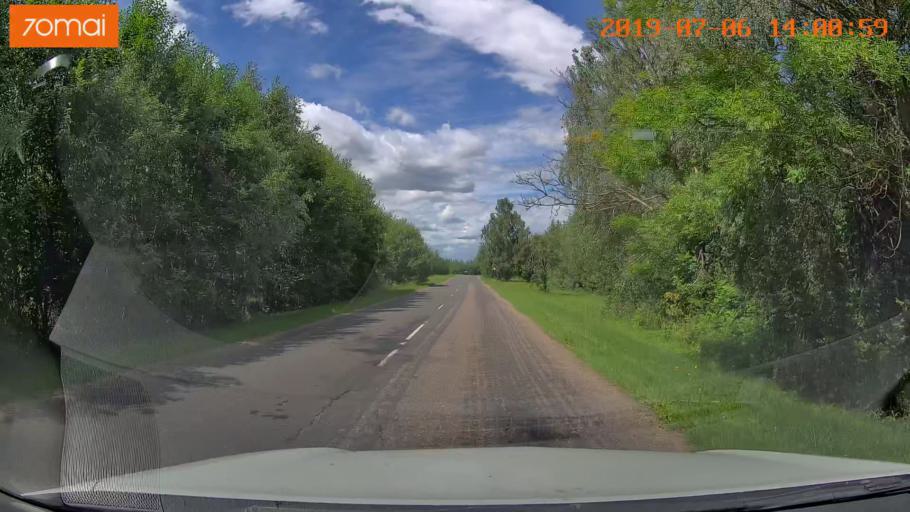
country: BY
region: Minsk
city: Ivyanyets
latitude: 53.8037
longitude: 26.8172
